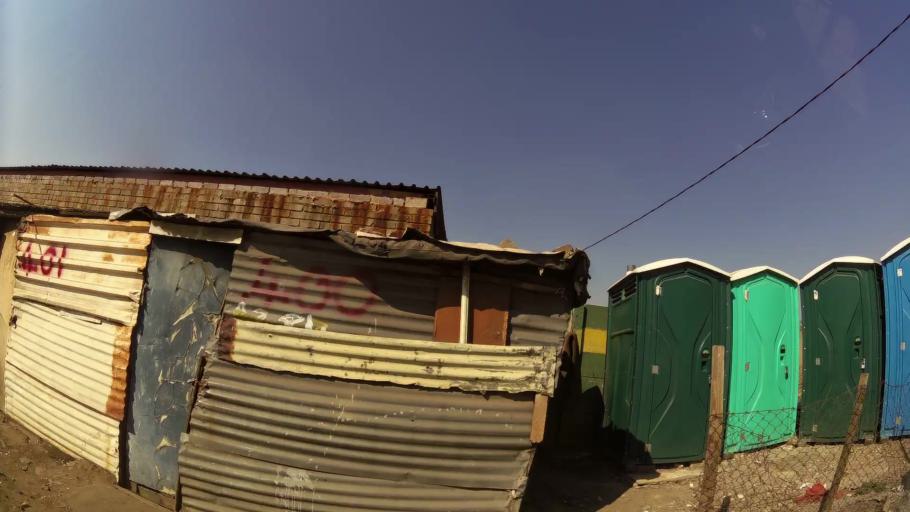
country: ZA
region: Gauteng
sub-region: Ekurhuleni Metropolitan Municipality
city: Boksburg
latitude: -26.2159
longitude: 28.2957
